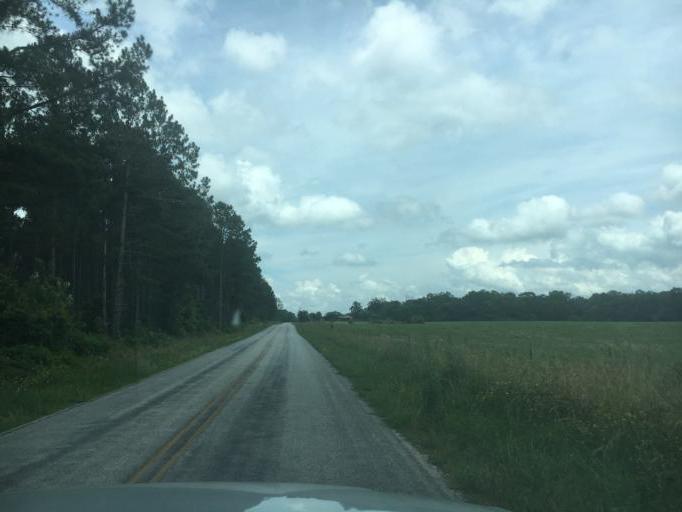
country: US
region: Georgia
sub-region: Hart County
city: Reed Creek
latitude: 34.4263
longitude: -82.9488
